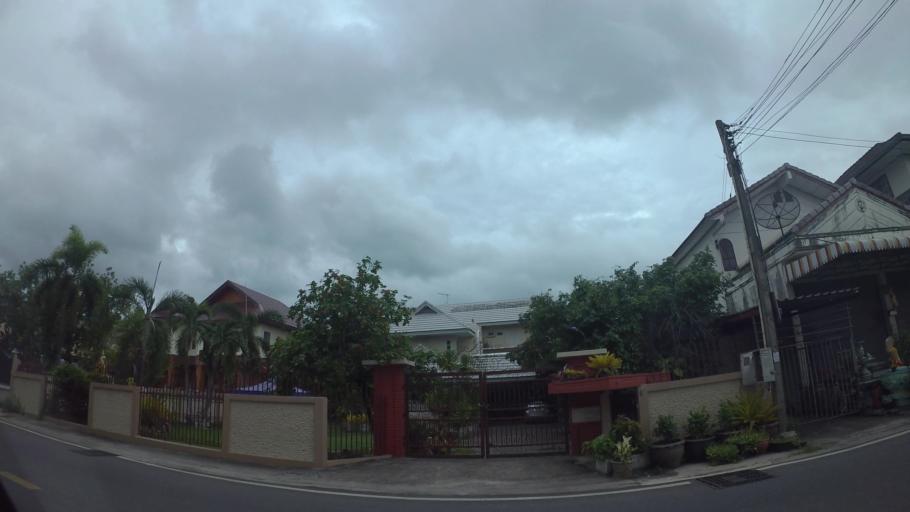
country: TH
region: Rayong
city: Rayong
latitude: 12.6652
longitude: 101.2699
